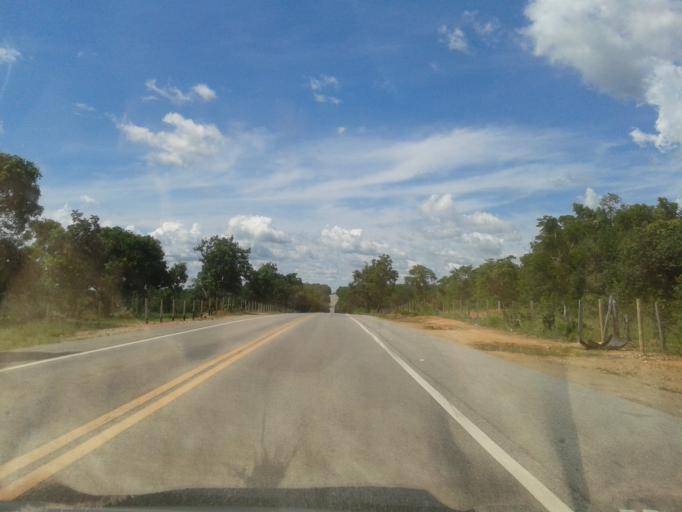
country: BR
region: Goias
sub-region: Goias
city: Goias
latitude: -15.7366
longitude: -50.1836
